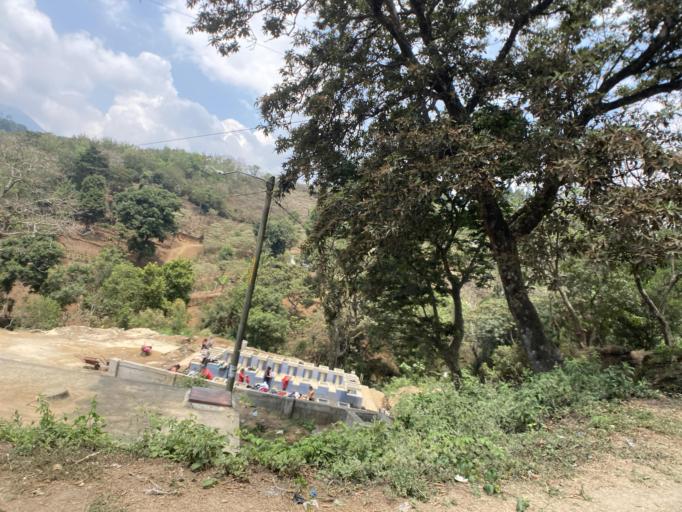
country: GT
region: Guatemala
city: Villa Canales
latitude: 14.4002
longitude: -90.5441
